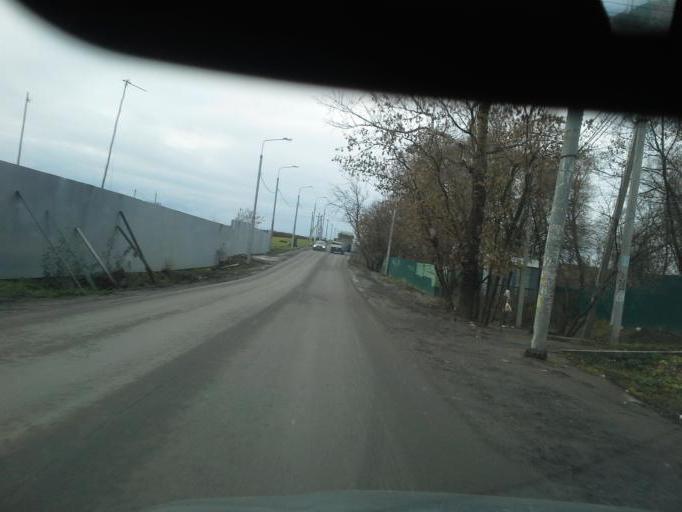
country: RU
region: Moskovskaya
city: Kommunarka
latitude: 55.5569
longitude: 37.4329
